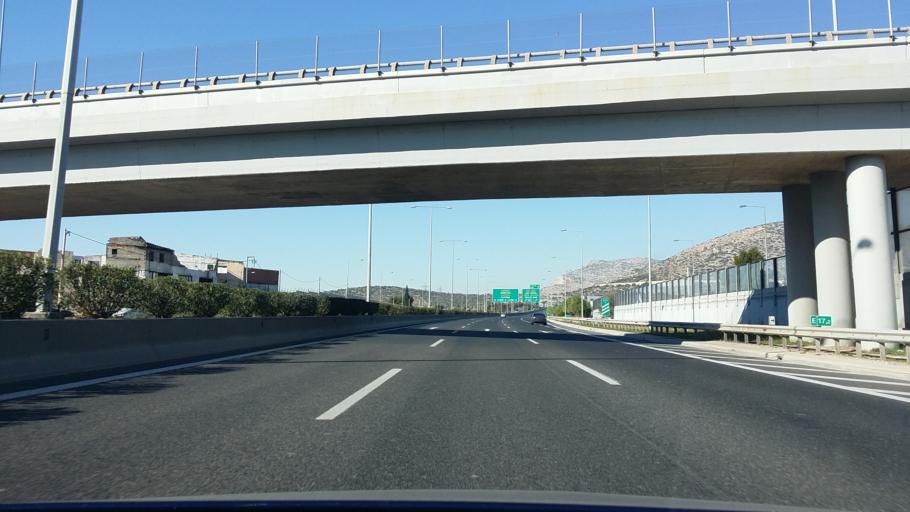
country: GR
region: Attica
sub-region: Nomarchia Dytikis Attikis
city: Ano Liosia
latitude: 38.0752
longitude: 23.6859
